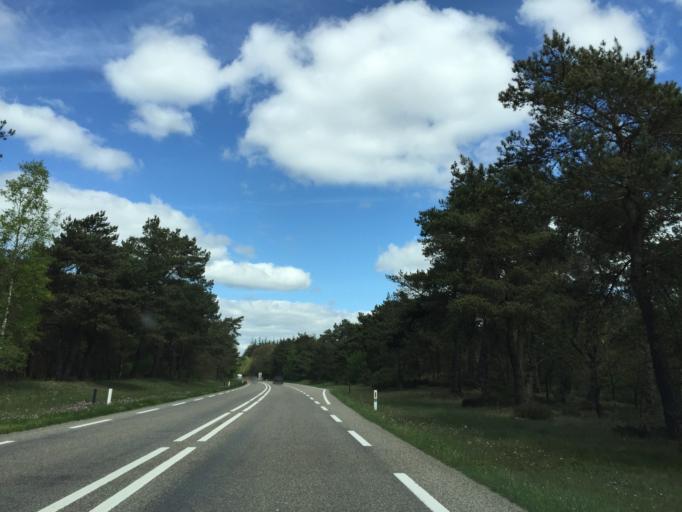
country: NL
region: Gelderland
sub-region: Gemeente Apeldoorn
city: Uddel
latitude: 52.2118
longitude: 5.7804
